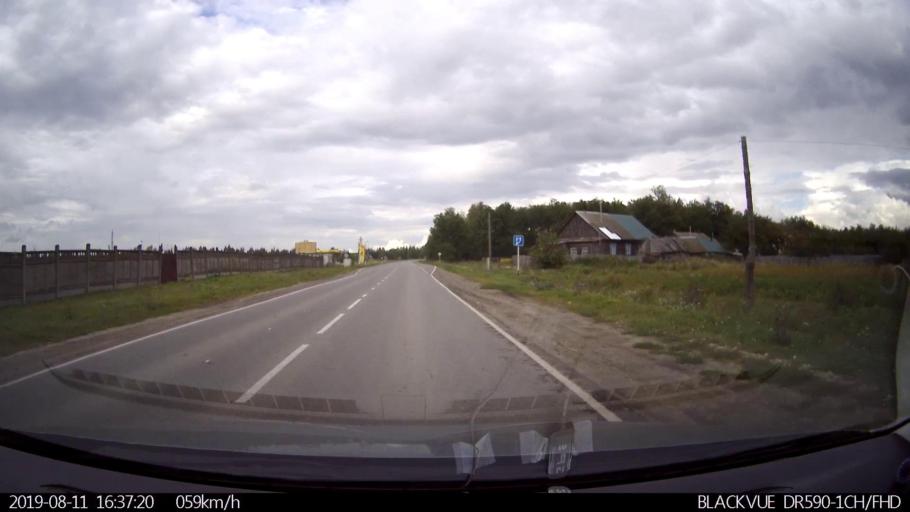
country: RU
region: Ulyanovsk
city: Mayna
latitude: 54.1265
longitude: 47.6138
